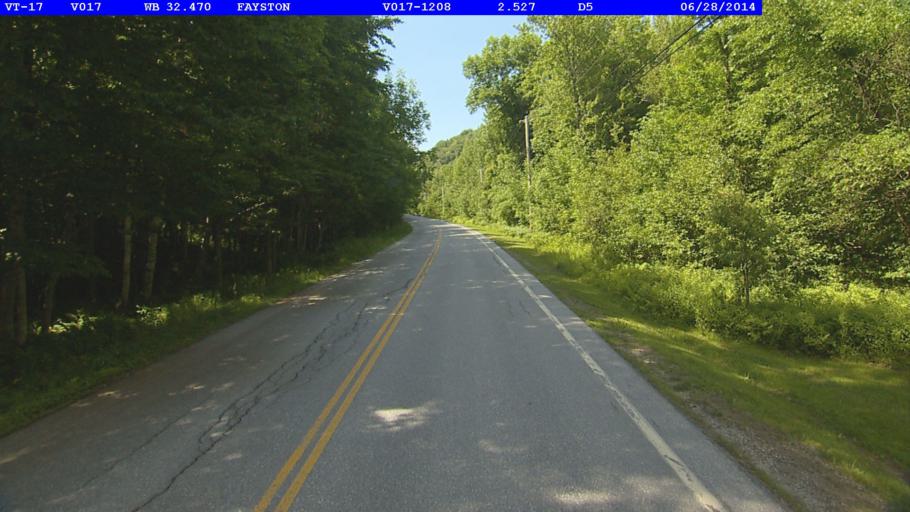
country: US
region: Vermont
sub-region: Washington County
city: Waterbury
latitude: 44.2014
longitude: -72.8955
